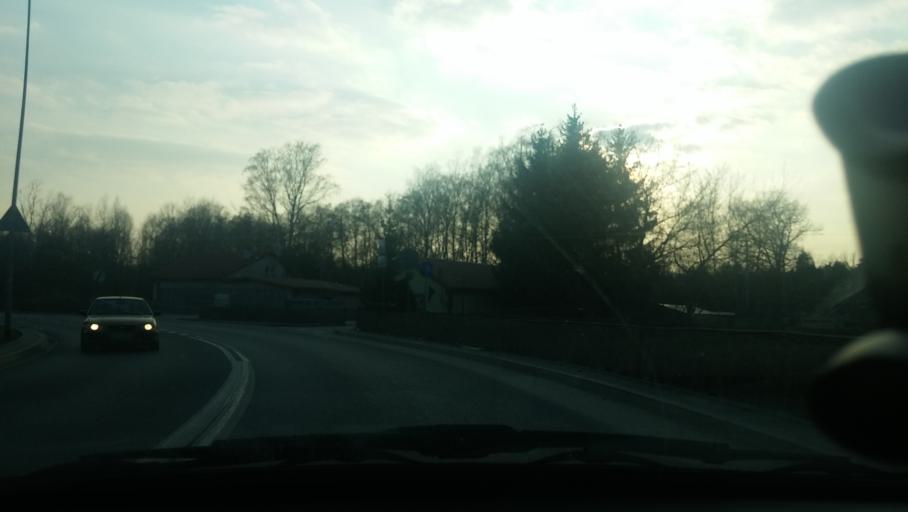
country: PL
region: Masovian Voivodeship
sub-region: Warszawa
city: Wesola
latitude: 52.2178
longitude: 21.2189
